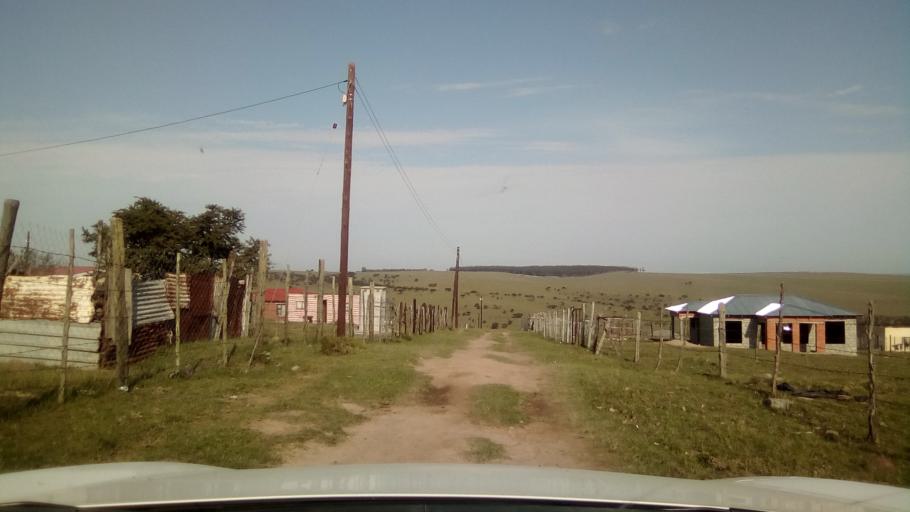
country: ZA
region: Eastern Cape
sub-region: Buffalo City Metropolitan Municipality
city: Bhisho
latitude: -32.9868
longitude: 27.2659
